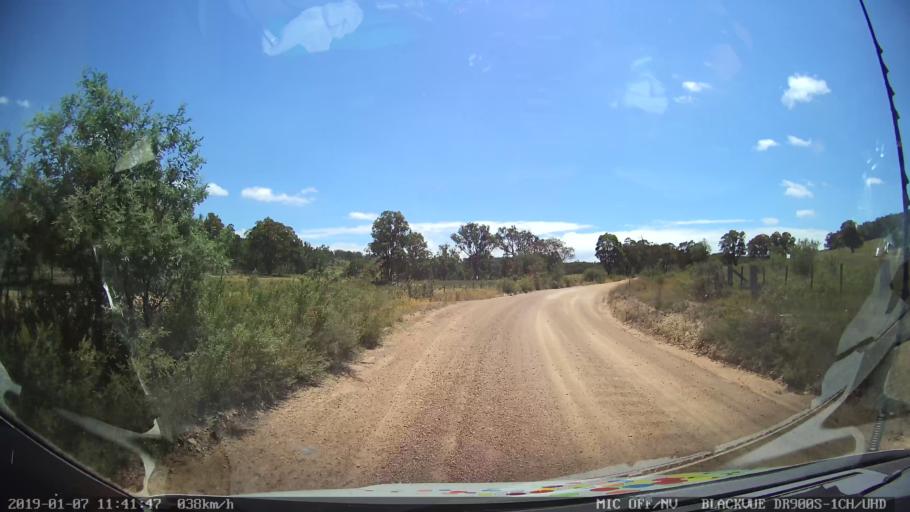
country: AU
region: New South Wales
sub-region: Guyra
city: Guyra
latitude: -30.3588
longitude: 151.5900
